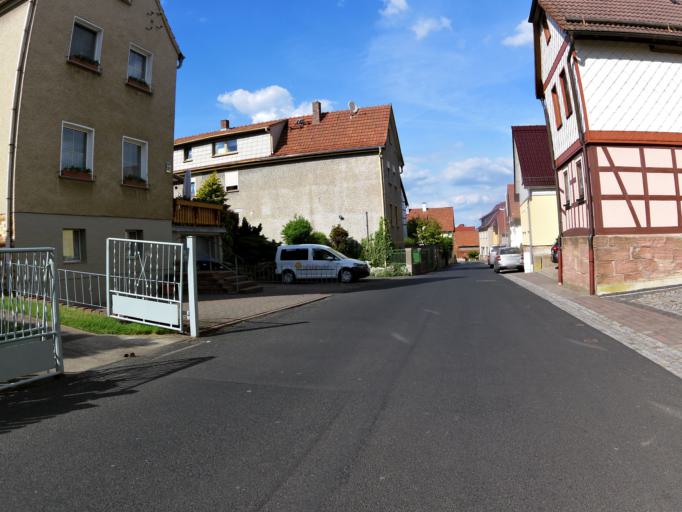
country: DE
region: Thuringia
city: Dermbach
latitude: 50.7141
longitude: 10.1139
